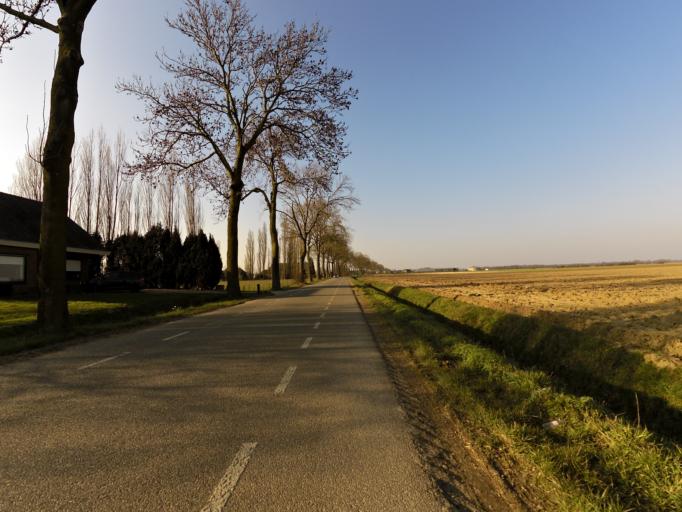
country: NL
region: Gelderland
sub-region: Gemeente Montferland
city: s-Heerenberg
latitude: 51.8616
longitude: 6.3072
